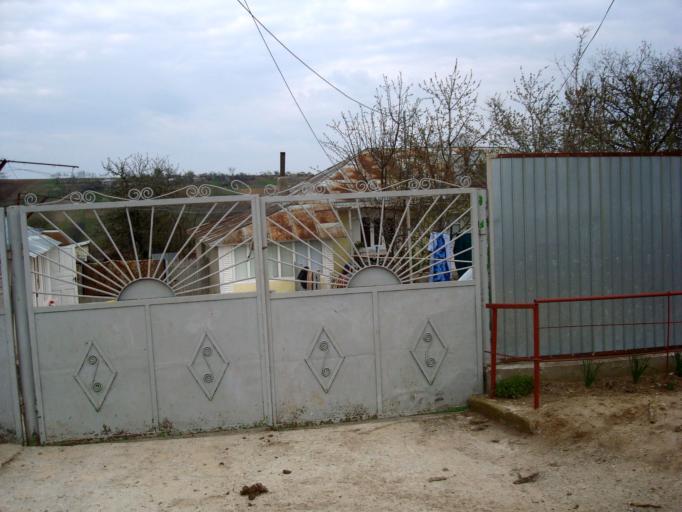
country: RO
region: Galati
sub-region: Comuna Radesti
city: Radesti
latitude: 46.0650
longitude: 27.7889
